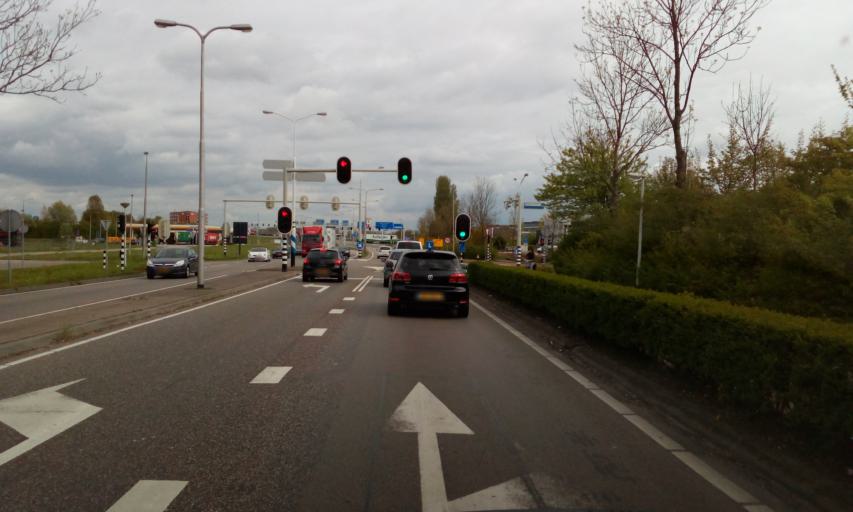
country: NL
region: South Holland
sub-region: Gemeente Barendrecht
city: Barendrecht
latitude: 51.8642
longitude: 4.5493
